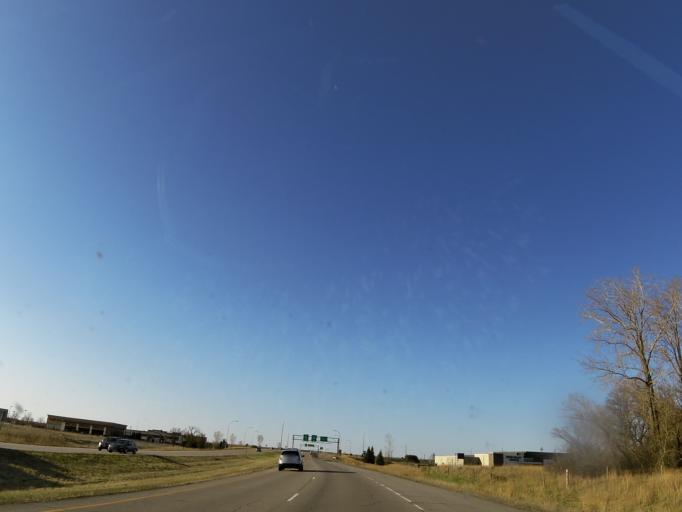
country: US
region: Minnesota
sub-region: Scott County
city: Prior Lake
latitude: 44.7793
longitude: -93.4140
